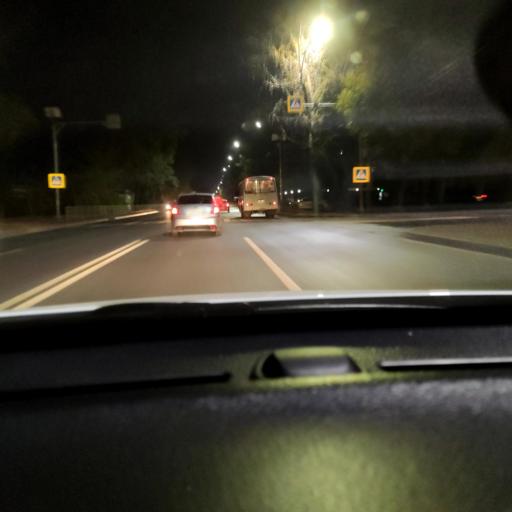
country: RU
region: Voronezj
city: Somovo
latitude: 51.7146
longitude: 39.2749
